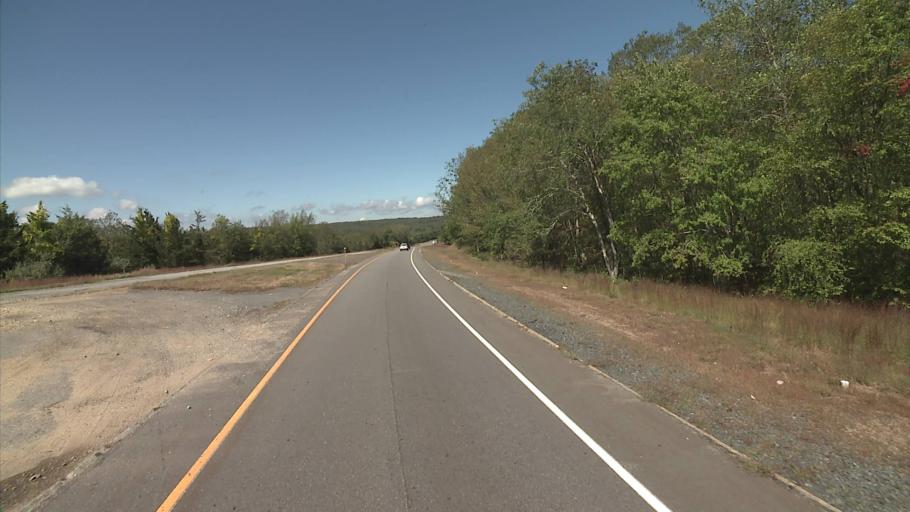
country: US
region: Connecticut
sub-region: New London County
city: Colchester
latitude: 41.4665
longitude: -72.2799
